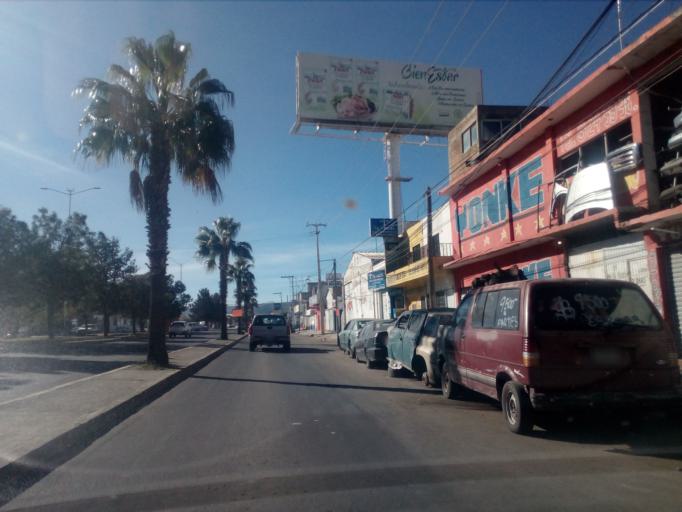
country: MX
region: Durango
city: Victoria de Durango
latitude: 23.9875
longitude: -104.6644
